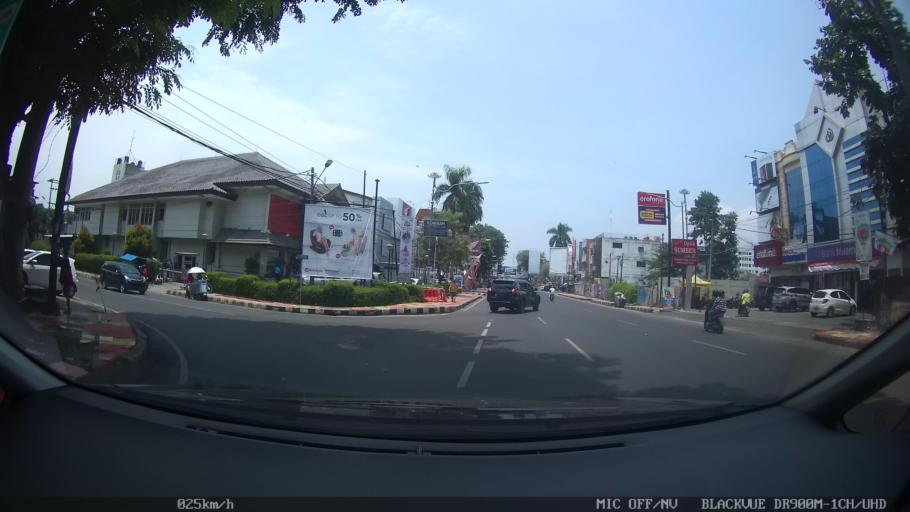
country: ID
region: Lampung
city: Bandarlampung
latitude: -5.4173
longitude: 105.2583
